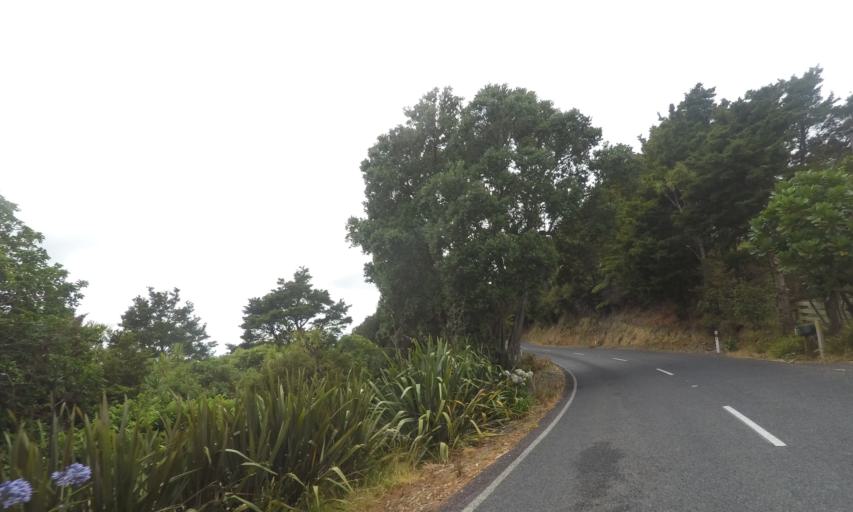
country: NZ
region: Northland
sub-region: Whangarei
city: Whangarei
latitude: -35.7573
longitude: 174.4515
